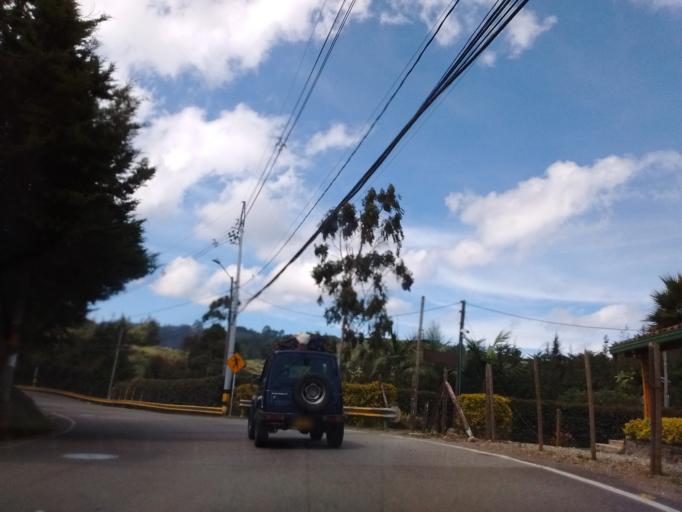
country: CO
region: Antioquia
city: Medellin
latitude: 6.2162
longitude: -75.5032
